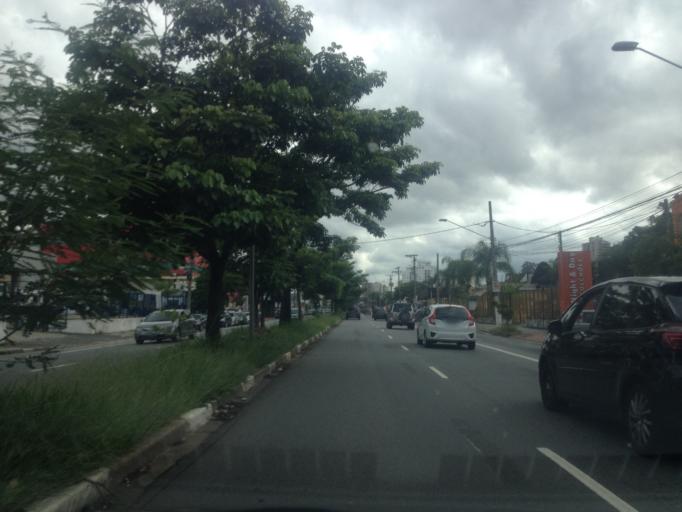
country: BR
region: Sao Paulo
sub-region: Osasco
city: Osasco
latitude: -23.5702
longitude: -46.7177
